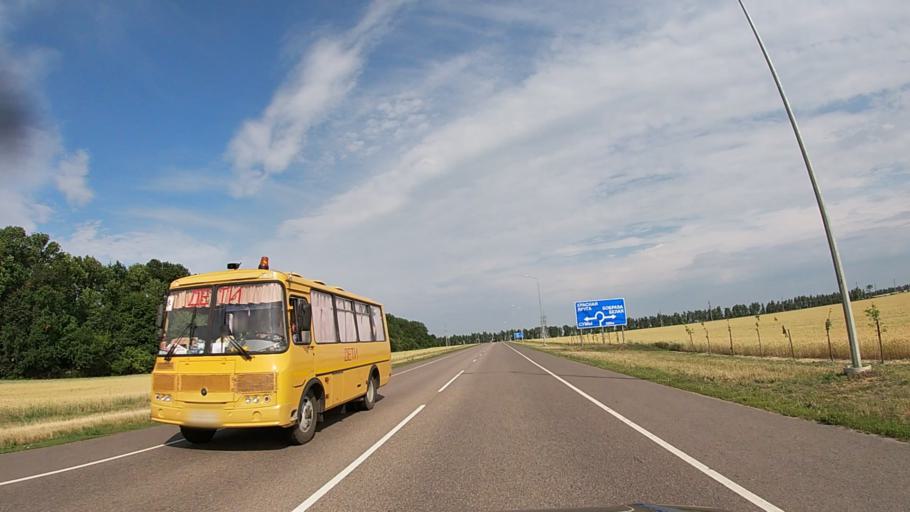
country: RU
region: Belgorod
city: Proletarskiy
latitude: 50.8290
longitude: 35.7725
